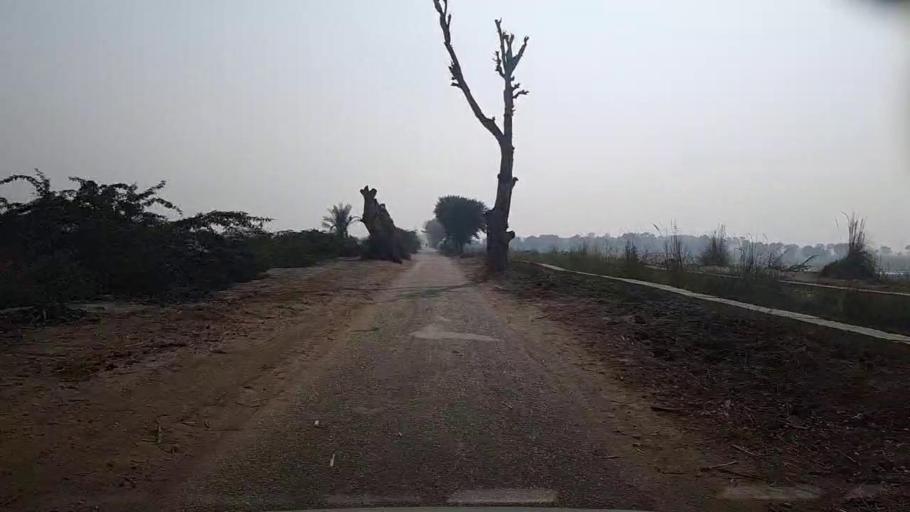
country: PK
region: Sindh
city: Setharja Old
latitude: 27.1072
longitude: 68.5082
